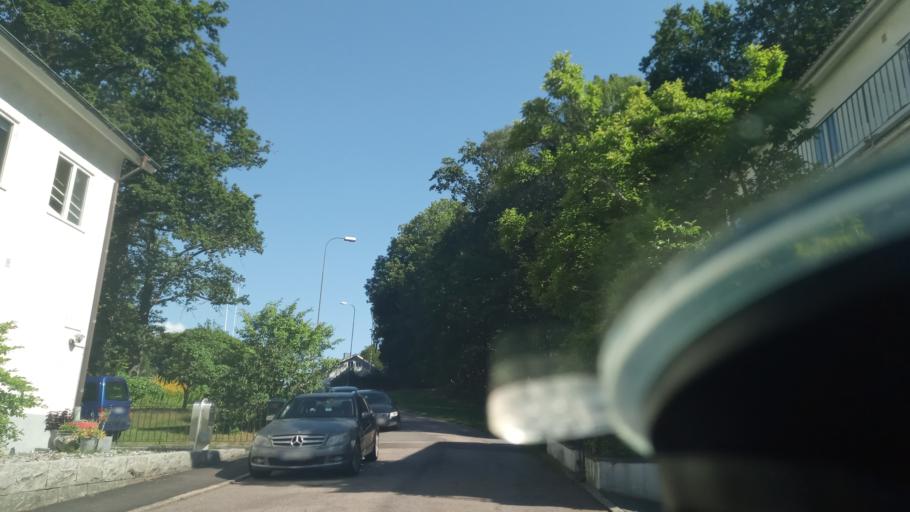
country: SE
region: Vaestra Goetaland
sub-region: Molndal
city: Moelndal
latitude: 57.6914
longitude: 12.0127
